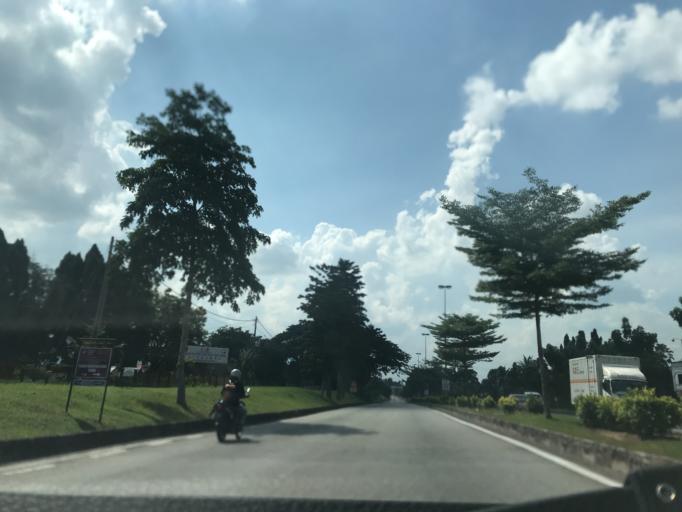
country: MY
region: Perak
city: Ipoh
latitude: 4.6319
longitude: 101.1147
